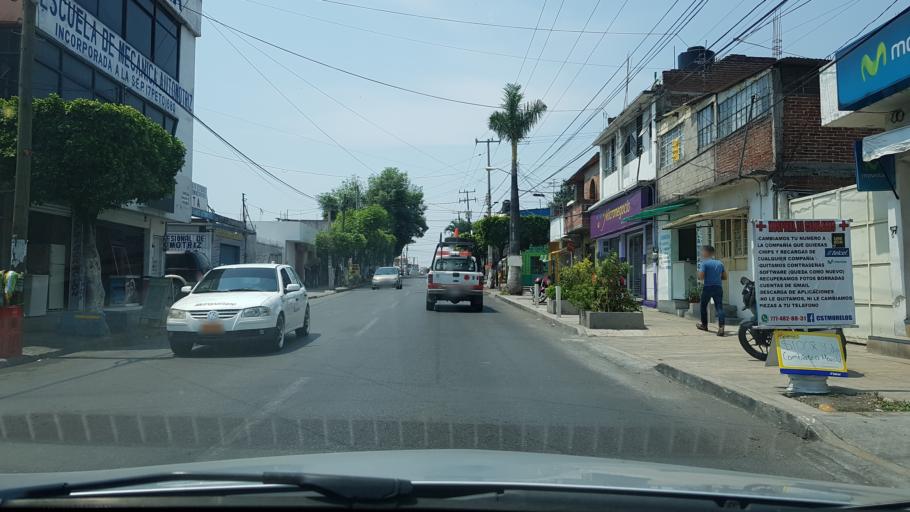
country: MX
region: Morelos
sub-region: Jiutepec
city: Jiutepec
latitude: 18.8956
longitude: -99.1702
